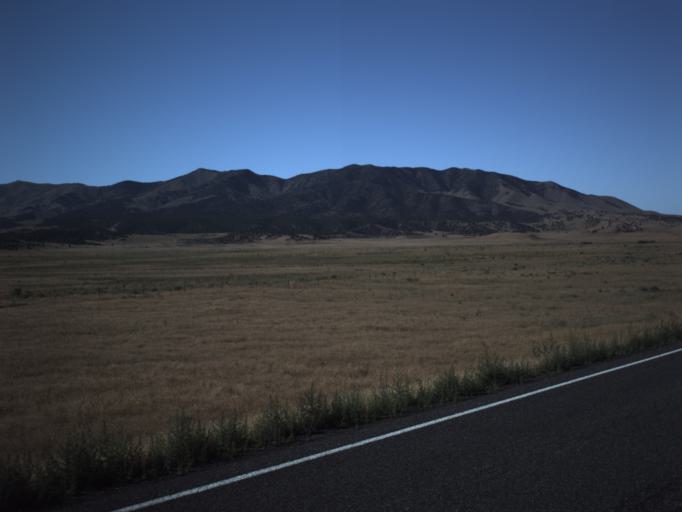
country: US
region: Utah
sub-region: Juab County
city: Mona
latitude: 39.6937
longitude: -112.2310
